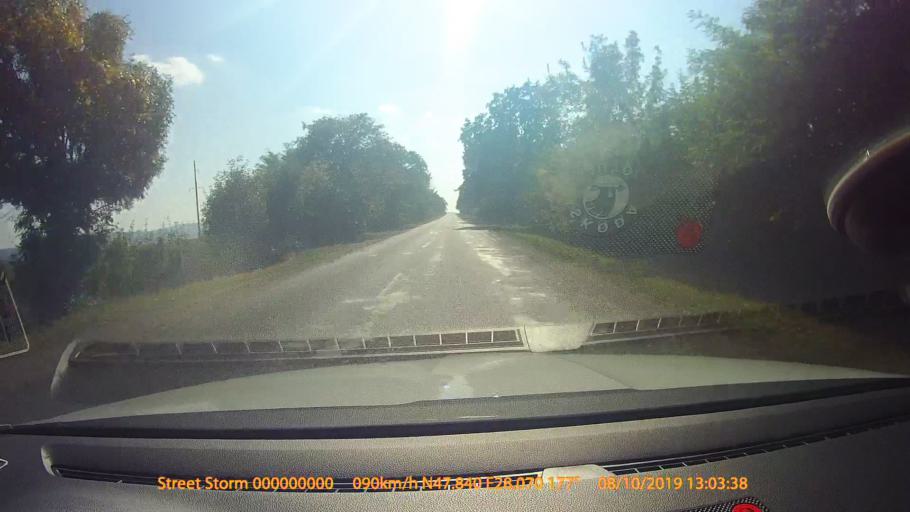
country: MD
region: Singerei
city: Biruinta
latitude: 47.8395
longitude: 28.0699
